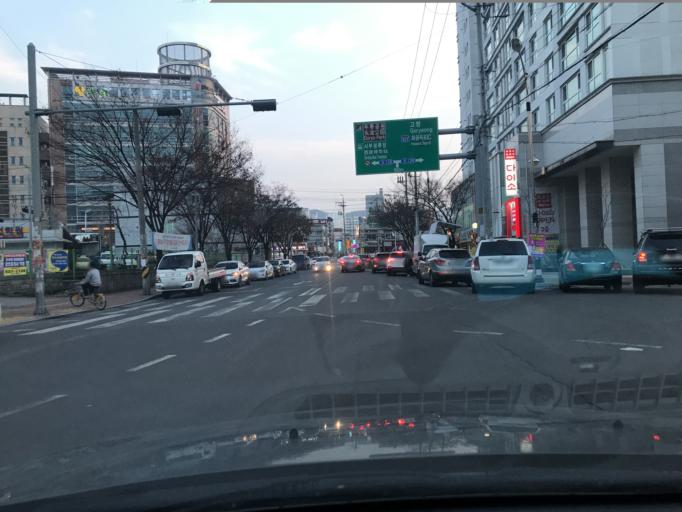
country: KR
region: Daegu
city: Hwawon
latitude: 35.8144
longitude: 128.5206
